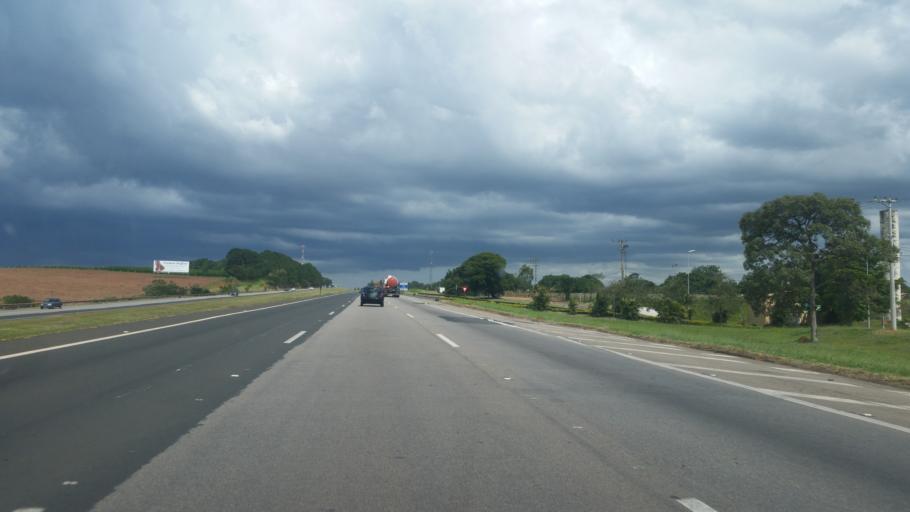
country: BR
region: Sao Paulo
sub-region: Boituva
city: Boituva
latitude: -23.2924
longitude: -47.7348
